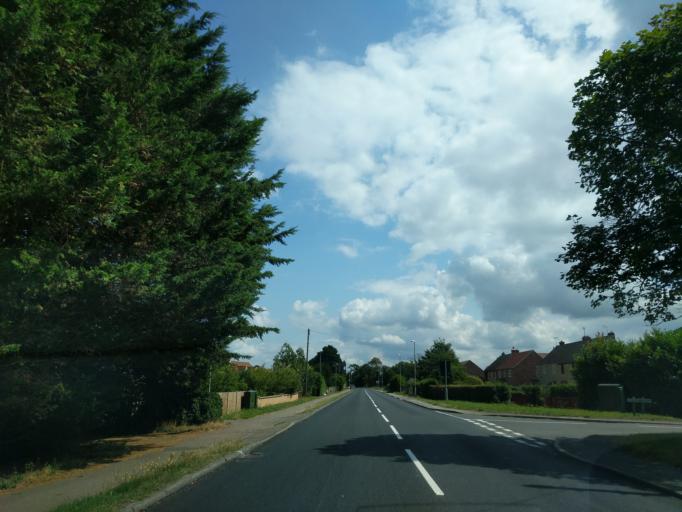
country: GB
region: England
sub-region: Cambridgeshire
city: Isleham
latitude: 52.3114
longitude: 0.4078
